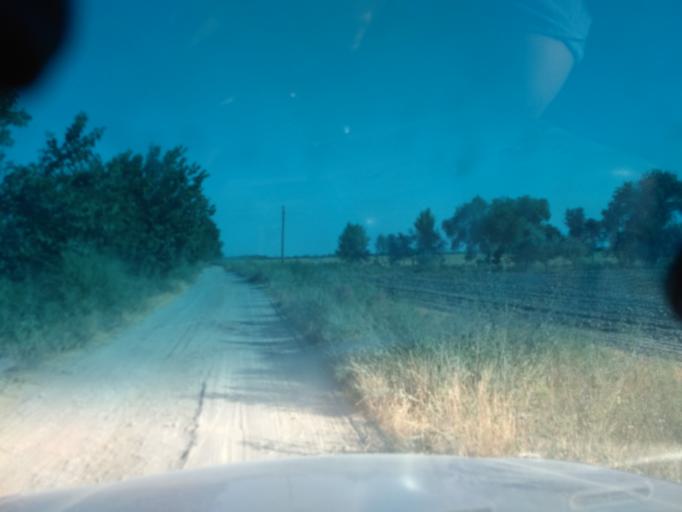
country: TJ
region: Viloyati Sughd
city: Buston
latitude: 40.5550
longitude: 69.0738
